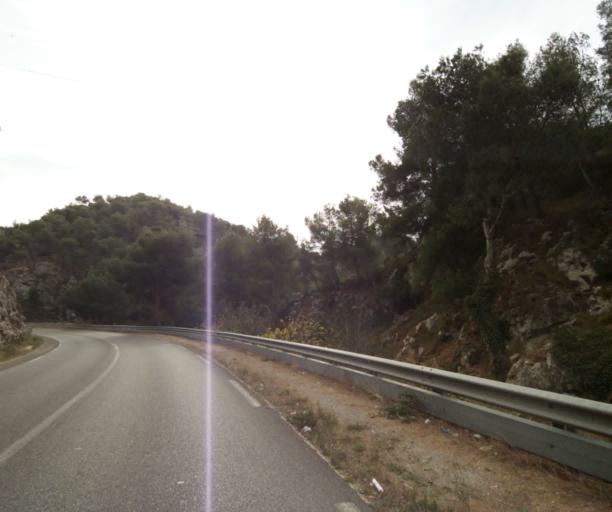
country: FR
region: Provence-Alpes-Cote d'Azur
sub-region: Departement des Bouches-du-Rhone
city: Le Rove
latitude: 43.3650
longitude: 5.2638
